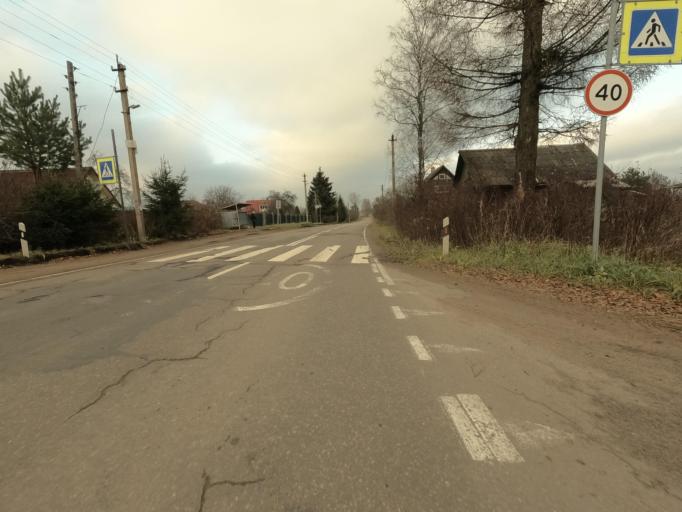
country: RU
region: Leningrad
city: Mga
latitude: 59.7742
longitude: 31.0241
